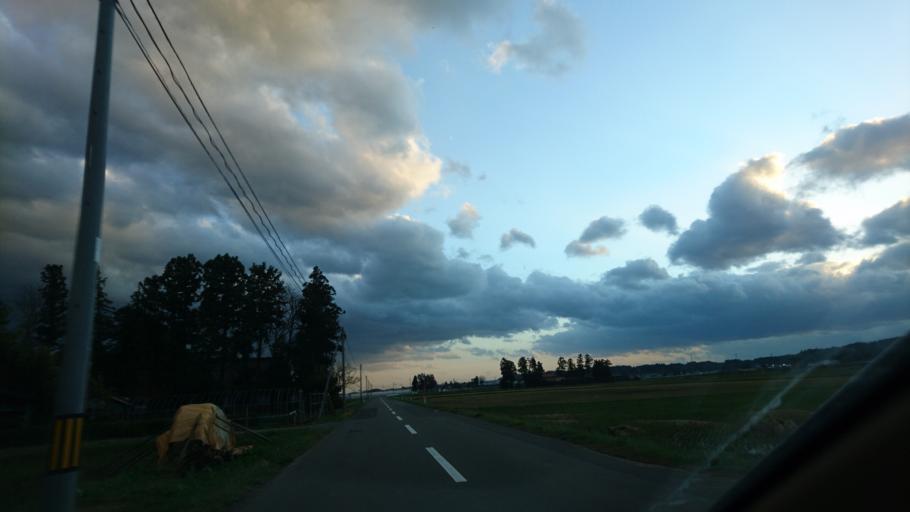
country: JP
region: Iwate
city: Mizusawa
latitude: 39.1095
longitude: 141.1502
